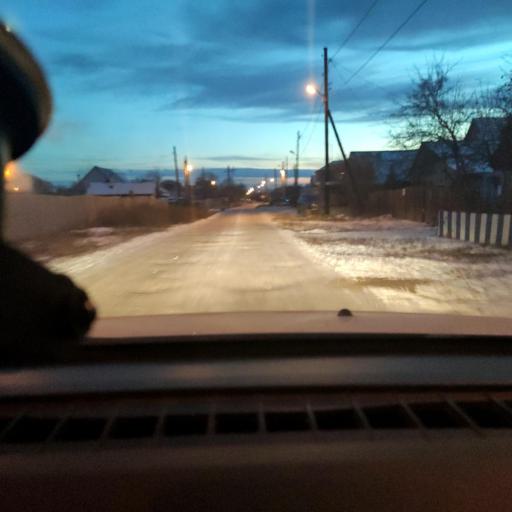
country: RU
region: Samara
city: Smyshlyayevka
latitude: 53.2554
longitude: 50.3555
